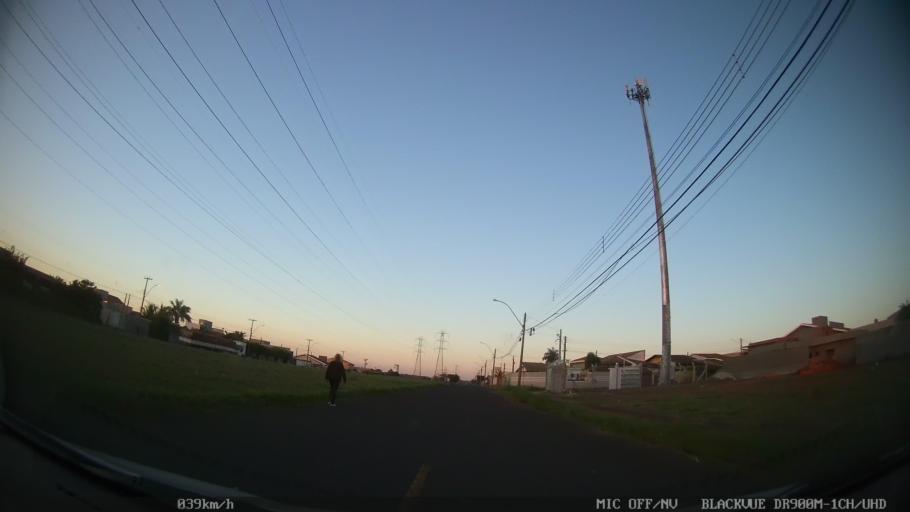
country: BR
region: Sao Paulo
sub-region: Sao Jose Do Rio Preto
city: Sao Jose do Rio Preto
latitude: -20.7972
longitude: -49.3490
